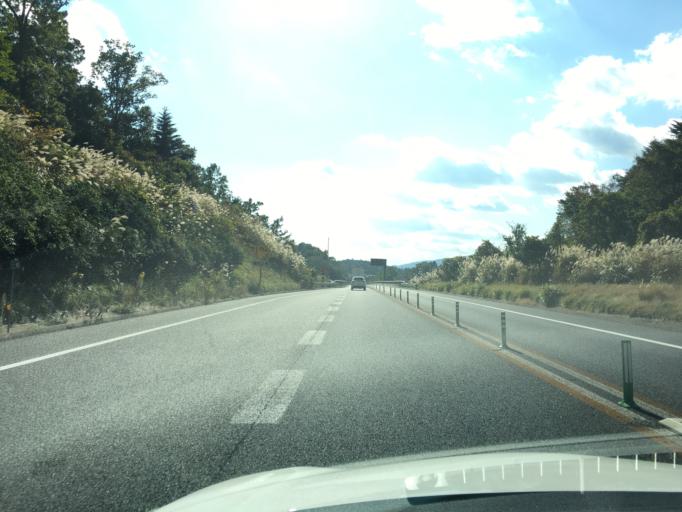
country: JP
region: Fukushima
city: Iwaki
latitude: 37.2347
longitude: 140.9819
